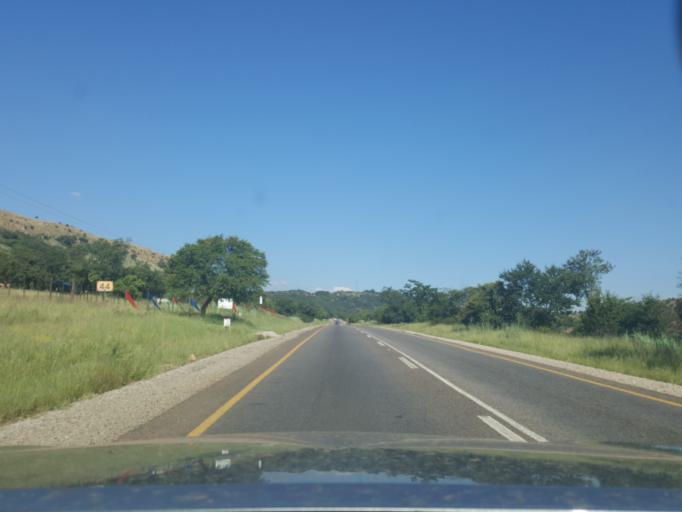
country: ZA
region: Gauteng
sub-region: City of Tshwane Metropolitan Municipality
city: Cullinan
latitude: -25.7765
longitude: 28.4690
